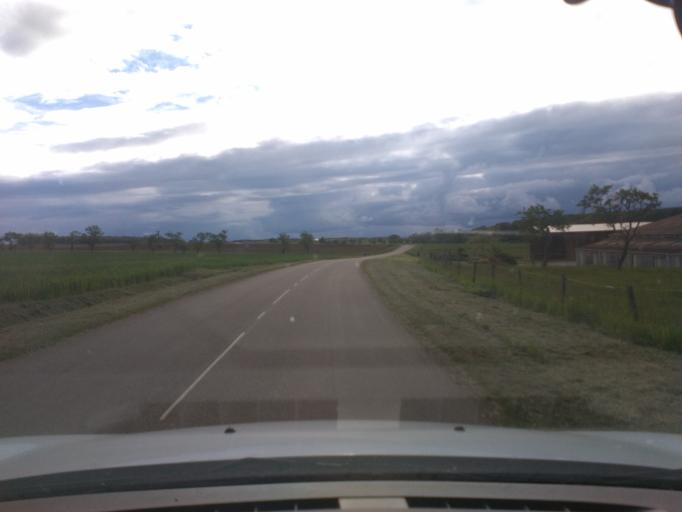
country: FR
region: Lorraine
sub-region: Departement des Vosges
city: Mirecourt
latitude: 48.3299
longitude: 6.0530
